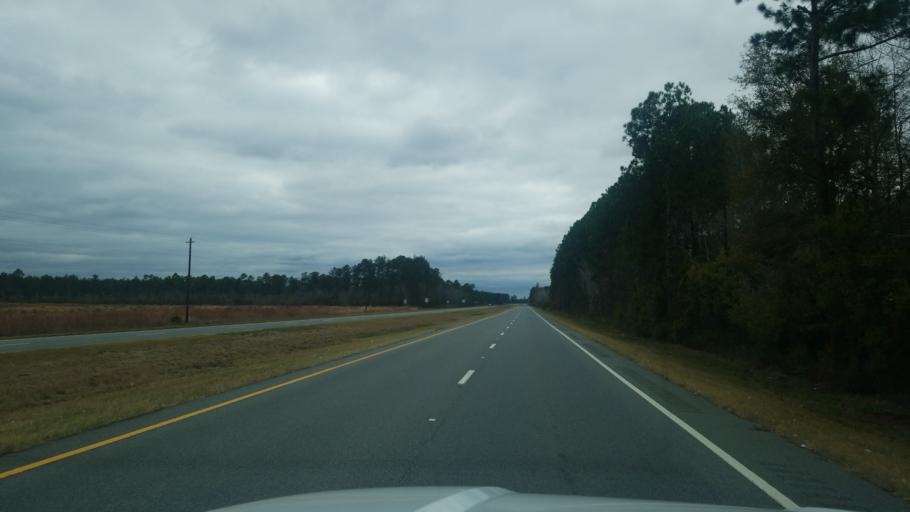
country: US
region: Georgia
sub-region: Pierce County
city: Blackshear
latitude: 31.1714
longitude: -82.2053
